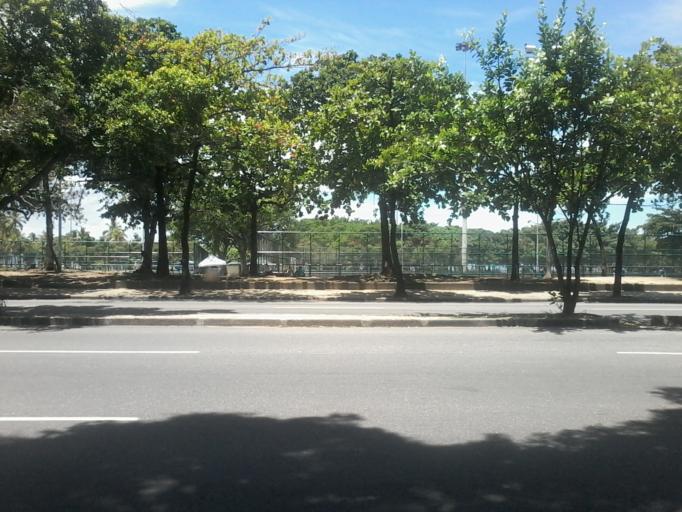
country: BR
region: Rio de Janeiro
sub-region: Rio De Janeiro
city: Rio de Janeiro
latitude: -22.9246
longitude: -43.1727
